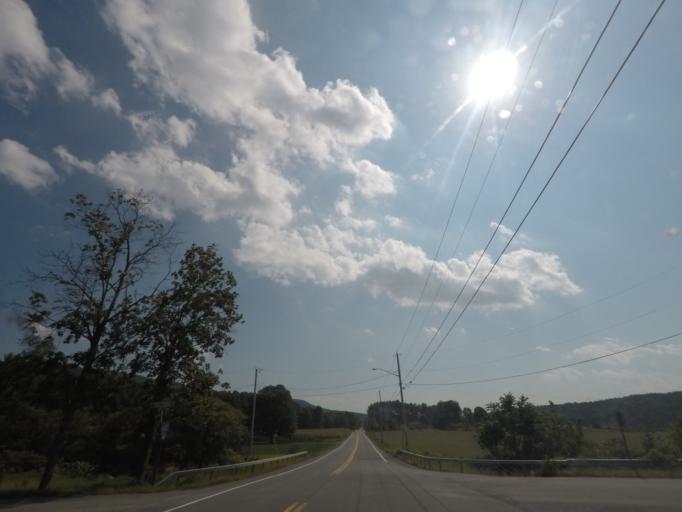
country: US
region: New York
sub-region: Rensselaer County
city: Poestenkill
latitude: 42.7899
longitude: -73.5328
